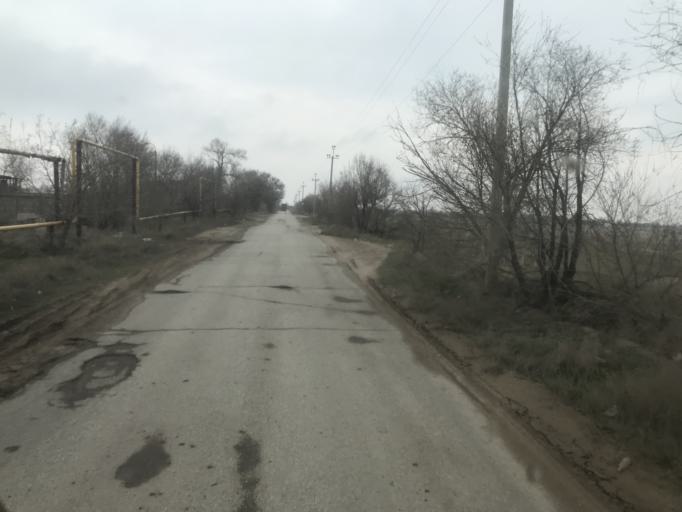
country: RU
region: Volgograd
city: Krasnoslobodsk
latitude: 48.5303
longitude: 44.6088
